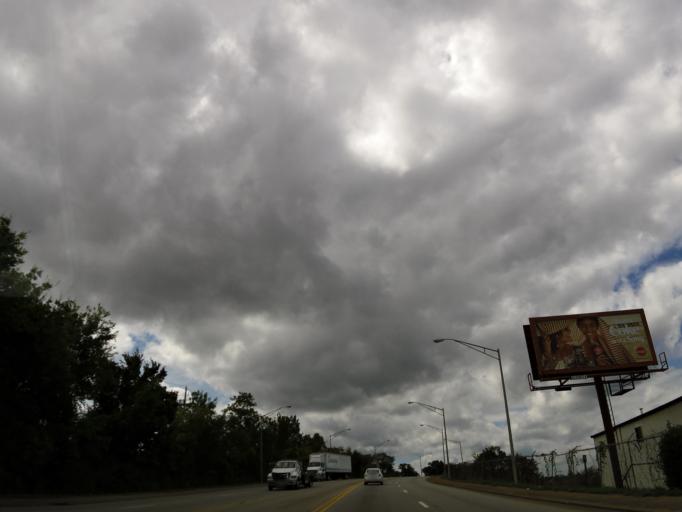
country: US
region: Tennessee
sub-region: Hamilton County
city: Chattanooga
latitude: 35.0237
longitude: -85.3117
